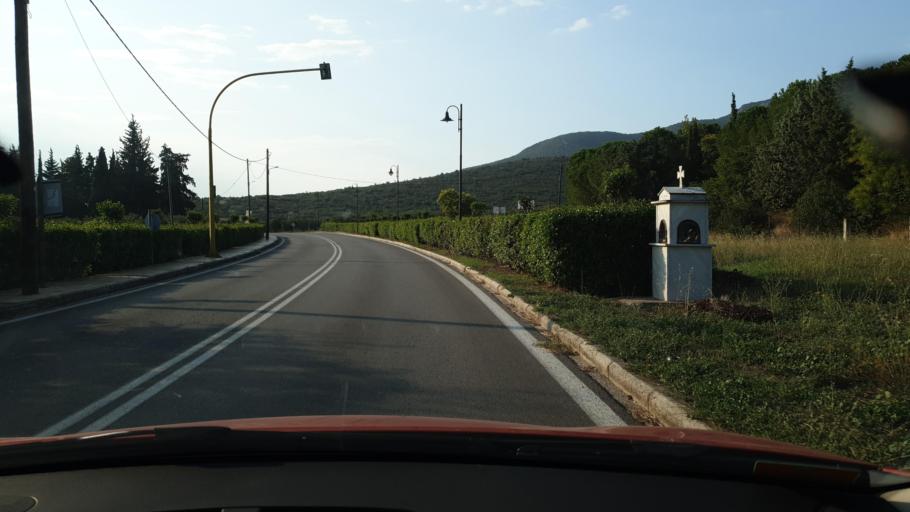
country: GR
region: Thessaly
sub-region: Nomos Magnisias
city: Sourpi
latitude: 39.1075
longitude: 22.8912
